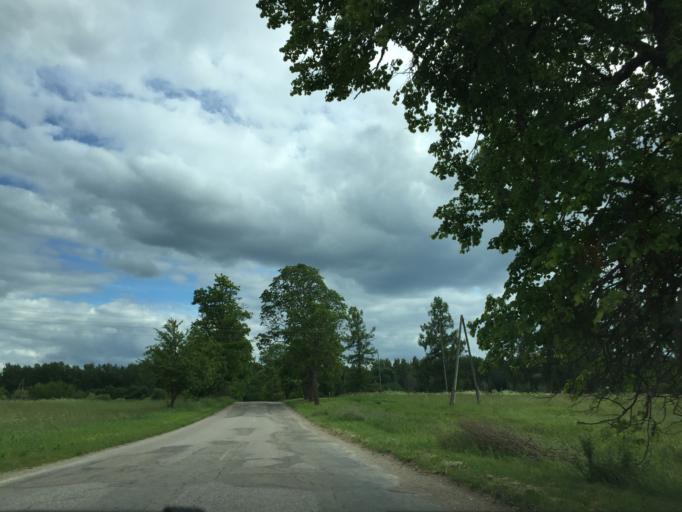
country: LV
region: Apes Novads
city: Ape
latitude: 57.5010
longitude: 26.4016
